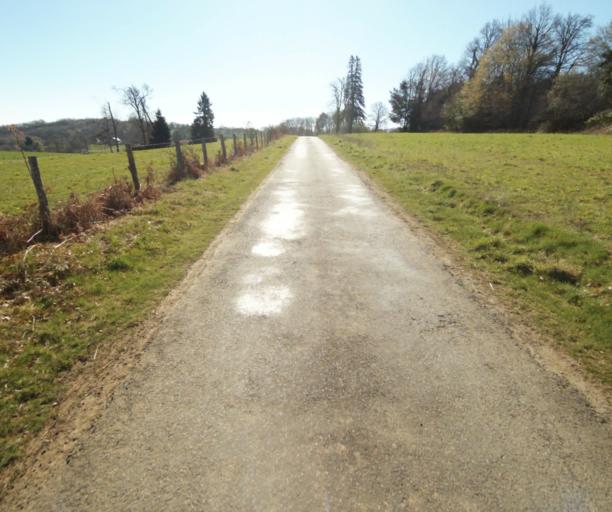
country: FR
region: Limousin
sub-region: Departement de la Correze
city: Chamboulive
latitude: 45.4130
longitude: 1.6894
